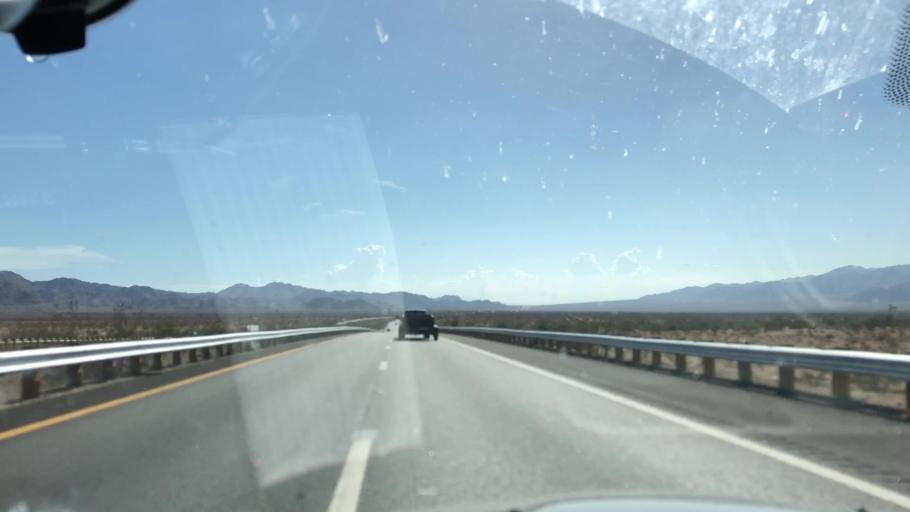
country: US
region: California
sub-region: Imperial County
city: Niland
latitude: 33.6762
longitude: -115.5707
